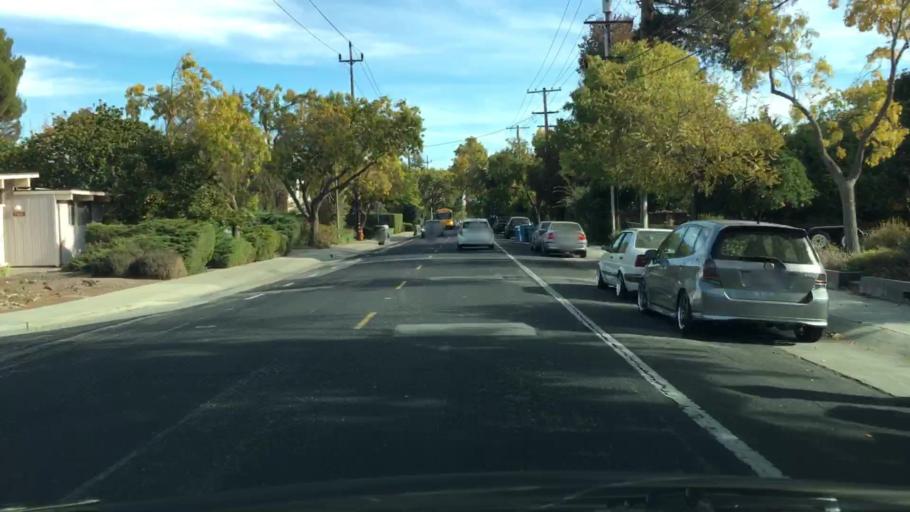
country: US
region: California
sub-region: Santa Clara County
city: Palo Alto
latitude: 37.4419
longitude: -122.1304
